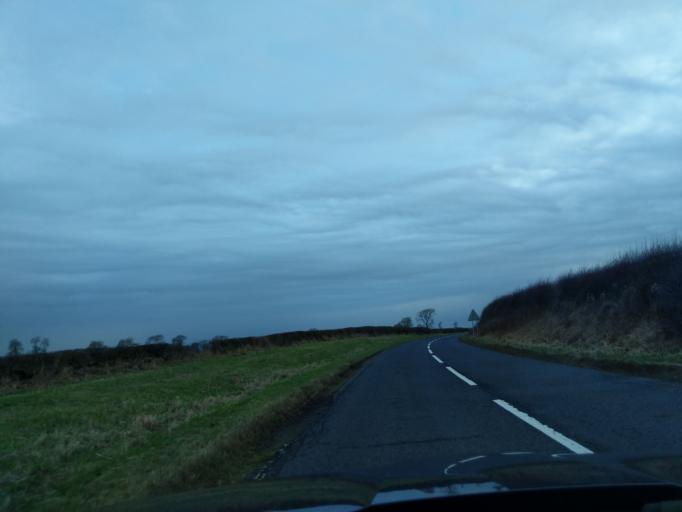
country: GB
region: England
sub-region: Northumberland
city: Rothley
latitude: 55.1315
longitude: -1.9576
